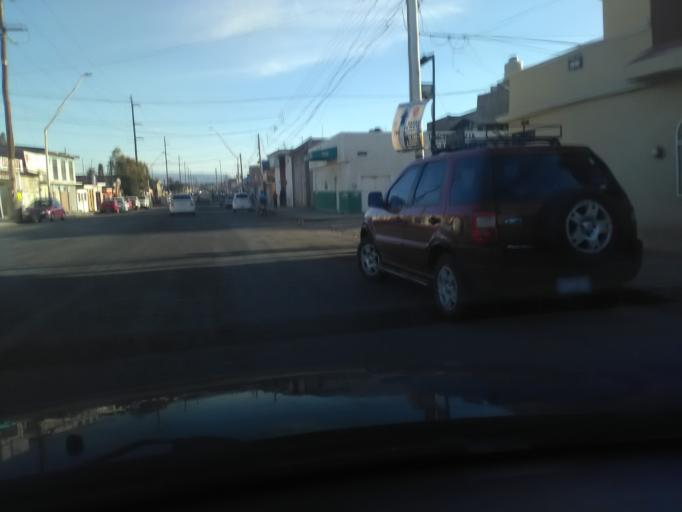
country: MX
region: Durango
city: Victoria de Durango
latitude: 24.0194
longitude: -104.6329
